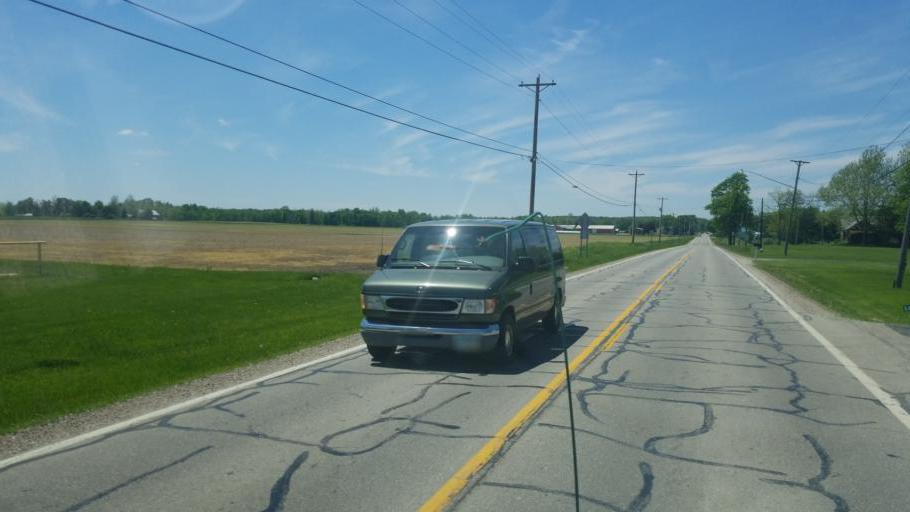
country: US
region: Ohio
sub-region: Huron County
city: Greenwich
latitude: 41.0301
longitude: -82.5297
